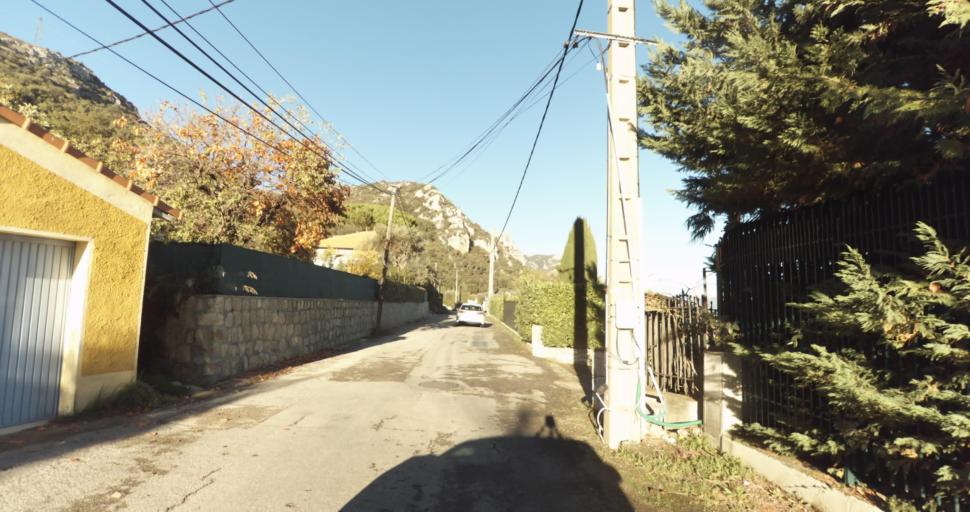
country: FR
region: Provence-Alpes-Cote d'Azur
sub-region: Departement des Alpes-Maritimes
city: Vence
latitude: 43.7351
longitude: 7.1187
